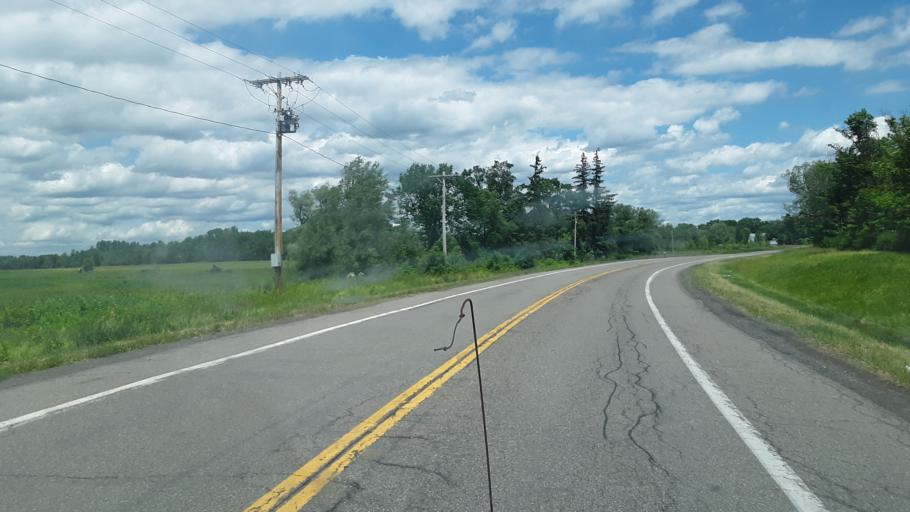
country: US
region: New York
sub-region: Madison County
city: Oneida
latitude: 43.1783
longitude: -75.6461
